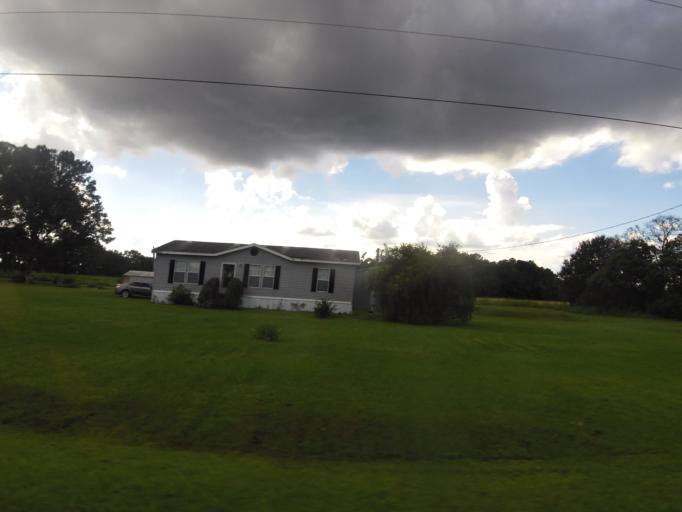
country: US
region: Florida
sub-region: Putnam County
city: East Palatka
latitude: 29.7629
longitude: -81.4756
